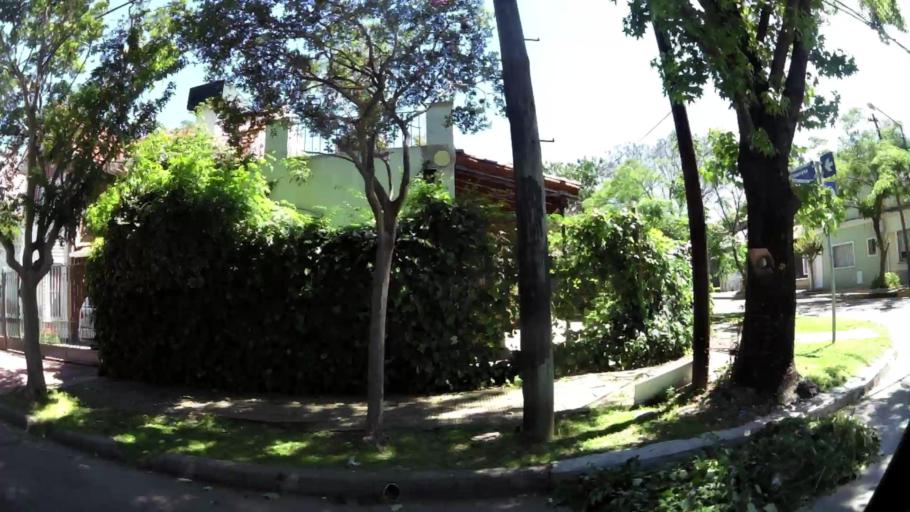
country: AR
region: Buenos Aires
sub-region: Partido de San Isidro
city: San Isidro
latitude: -34.4838
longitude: -58.5112
